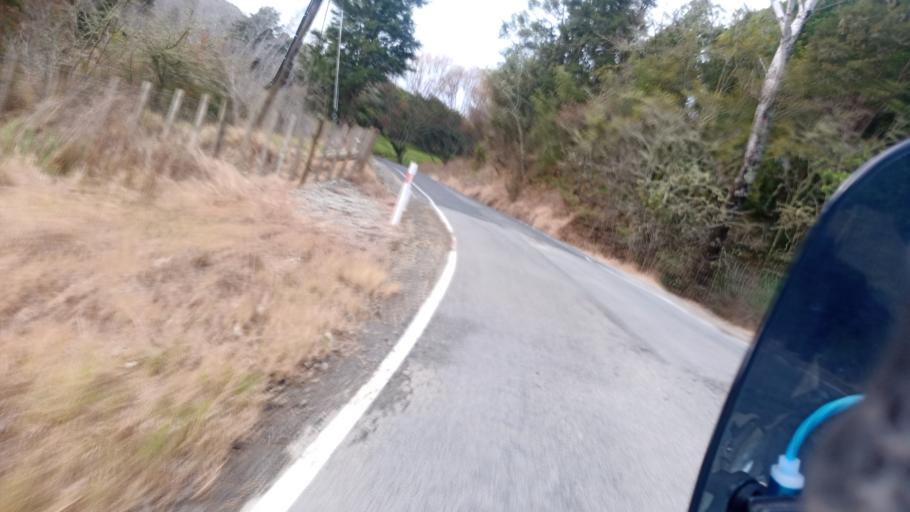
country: NZ
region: Gisborne
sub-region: Gisborne District
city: Gisborne
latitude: -38.4108
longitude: 177.9355
